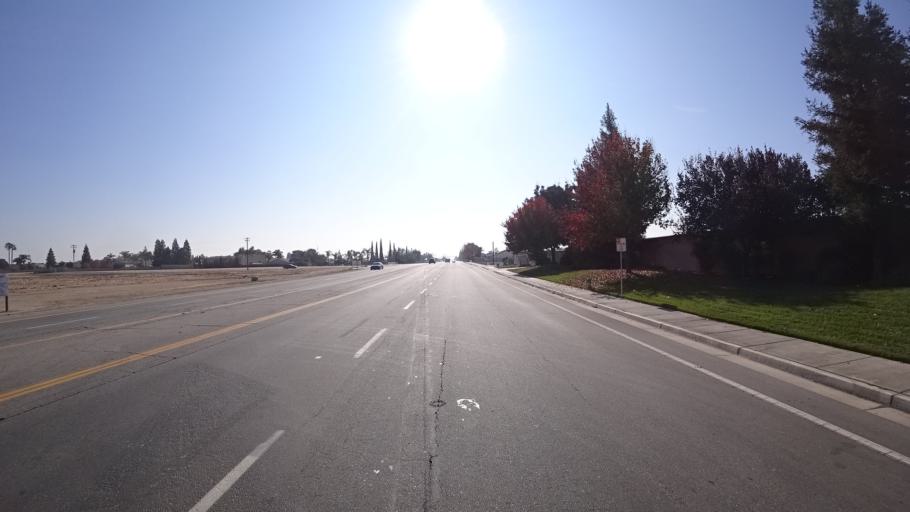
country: US
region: California
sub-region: Kern County
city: Greenfield
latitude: 35.2933
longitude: -119.0390
